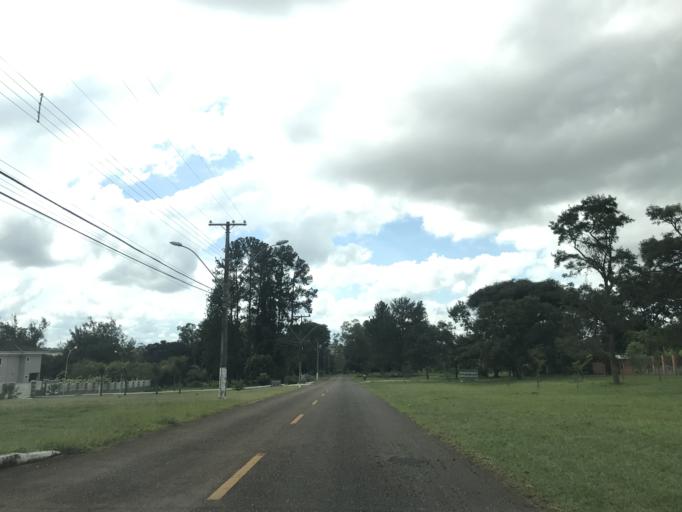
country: BR
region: Federal District
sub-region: Brasilia
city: Brasilia
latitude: -15.8898
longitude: -47.9247
